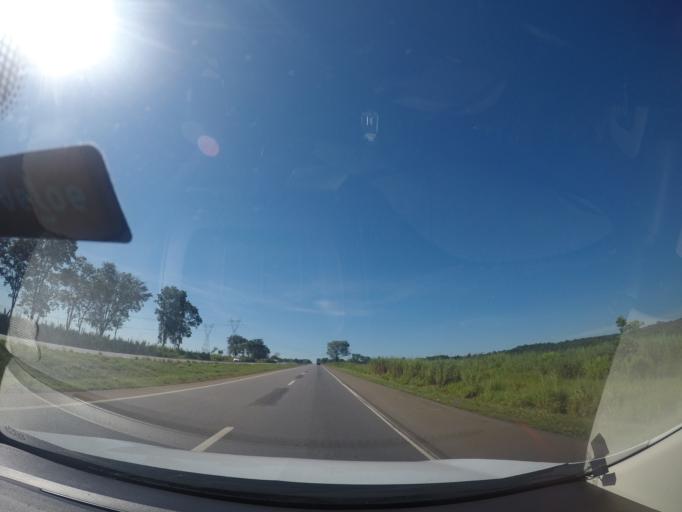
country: BR
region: Goias
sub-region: Morrinhos
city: Morrinhos
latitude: -17.5487
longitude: -49.2073
